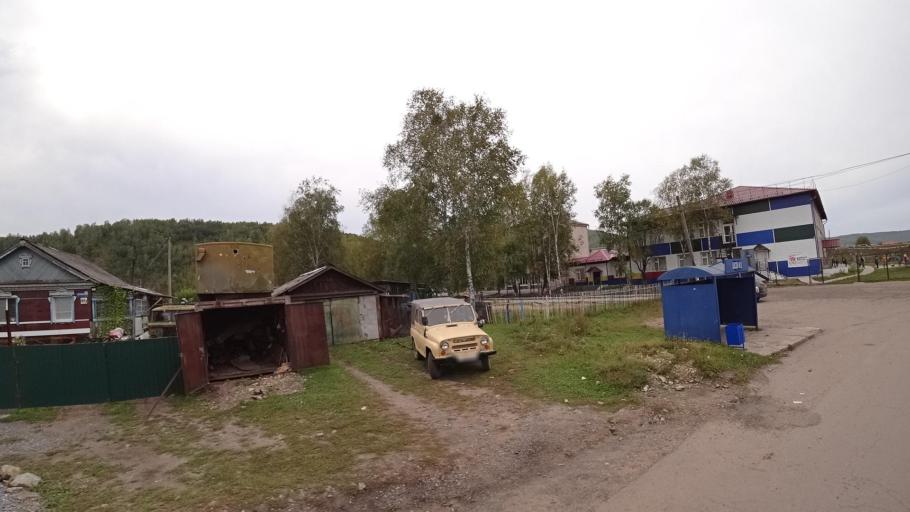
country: RU
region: Jewish Autonomous Oblast
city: Khingansk
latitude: 49.0278
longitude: 131.0491
